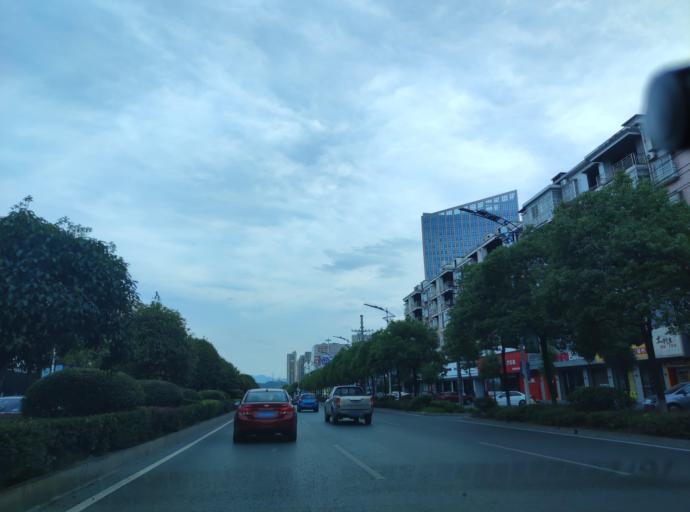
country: CN
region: Jiangxi Sheng
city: Pingxiang
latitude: 27.6392
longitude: 113.8705
